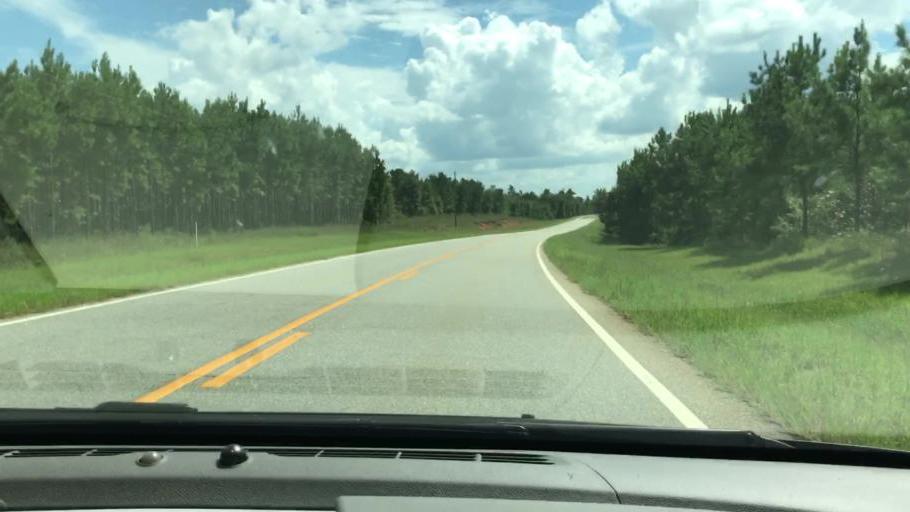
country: US
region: Georgia
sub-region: Quitman County
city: Georgetown
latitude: 31.9155
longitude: -85.0590
